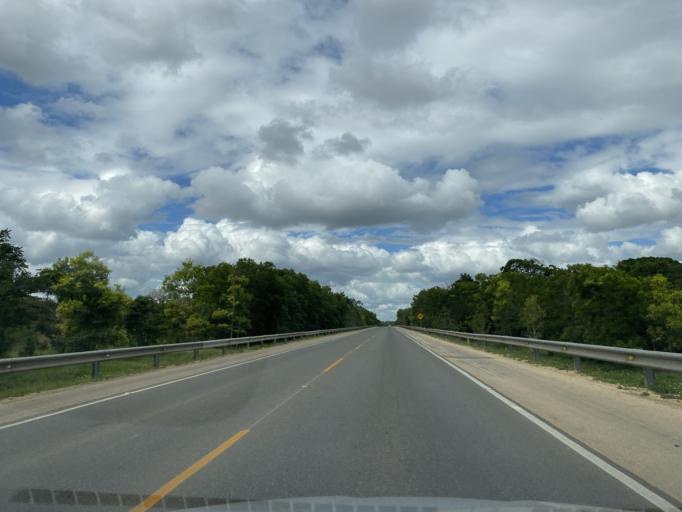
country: DO
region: Santo Domingo
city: Guerra
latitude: 18.5342
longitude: -69.7540
